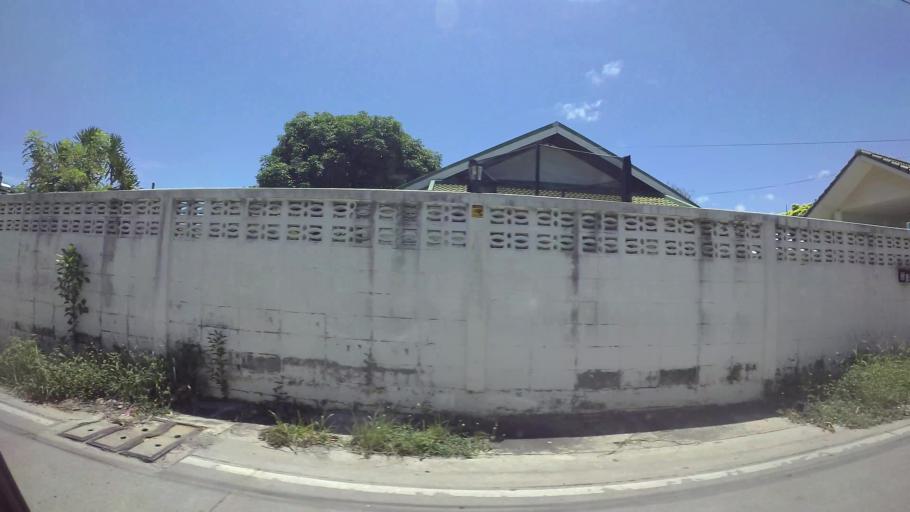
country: TH
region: Chon Buri
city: Phatthaya
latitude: 12.9425
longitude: 100.9021
